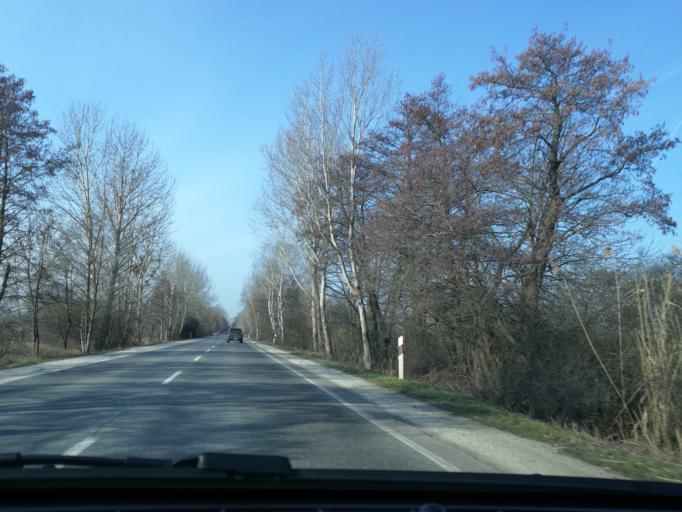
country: HU
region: Szabolcs-Szatmar-Bereg
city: Levelek
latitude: 47.9619
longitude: 21.9705
